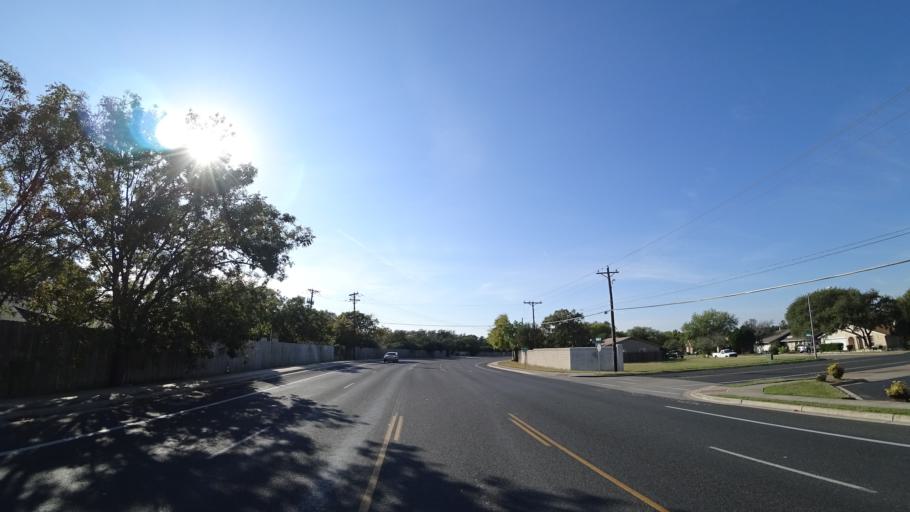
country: US
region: Texas
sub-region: Williamson County
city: Anderson Mill
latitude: 30.4469
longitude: -97.8117
